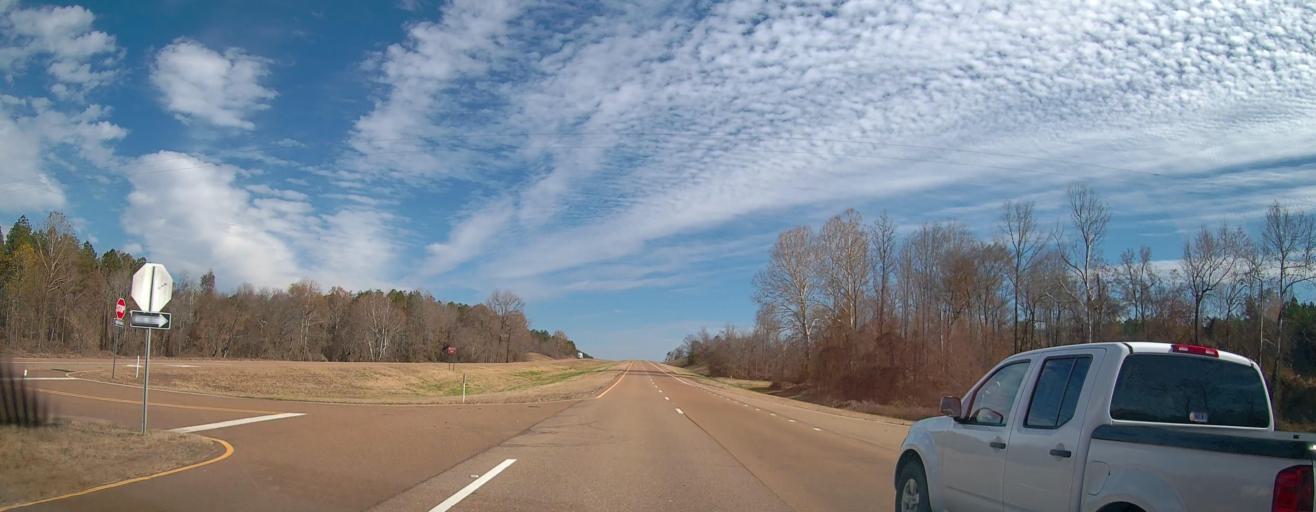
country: US
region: Mississippi
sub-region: Benton County
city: Ashland
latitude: 34.9485
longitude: -89.1053
